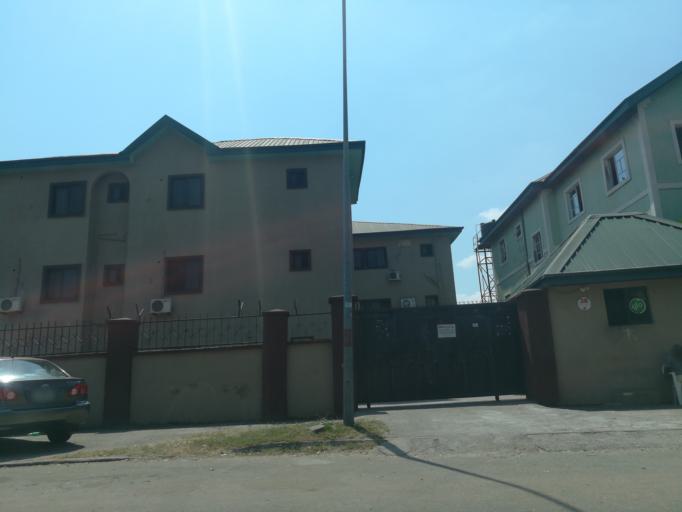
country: NG
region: Abuja Federal Capital Territory
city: Abuja
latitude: 9.0620
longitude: 7.4407
